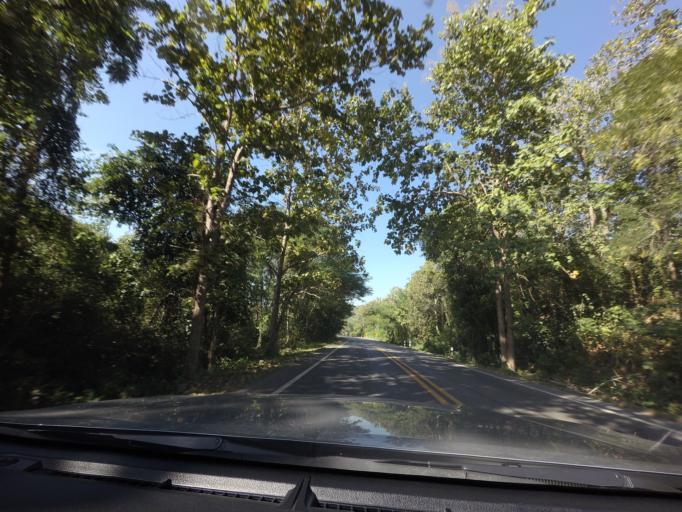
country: TH
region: Sukhothai
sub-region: Amphoe Si Satchanalai
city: Si Satchanalai
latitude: 17.6155
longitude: 99.7091
